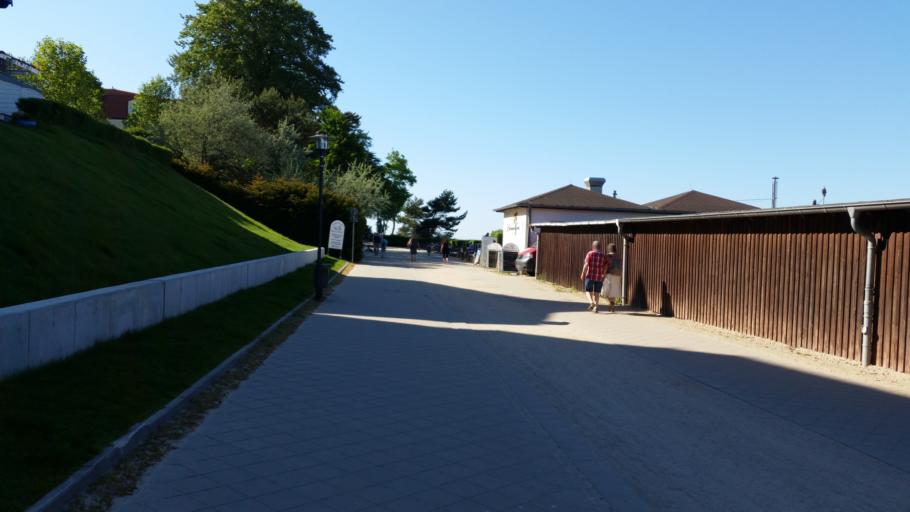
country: DE
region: Mecklenburg-Vorpommern
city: Seebad Bansin
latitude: 53.9759
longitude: 14.1412
